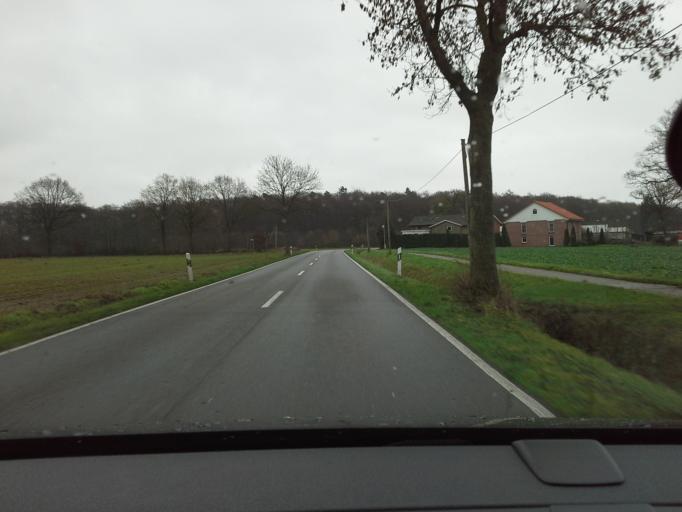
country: DE
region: Schleswig-Holstein
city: Bilsen
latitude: 53.7577
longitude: 9.8672
